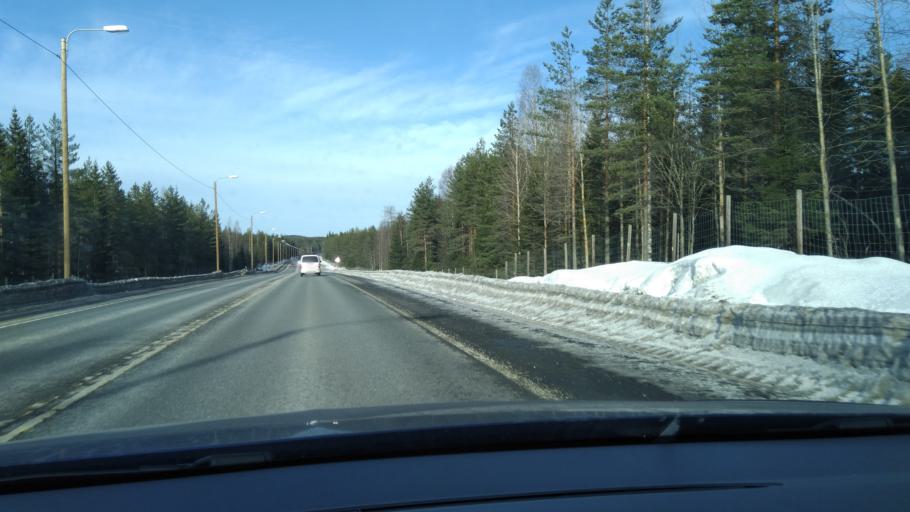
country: FI
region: Pirkanmaa
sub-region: Tampere
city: Orivesi
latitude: 61.6545
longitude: 24.2463
